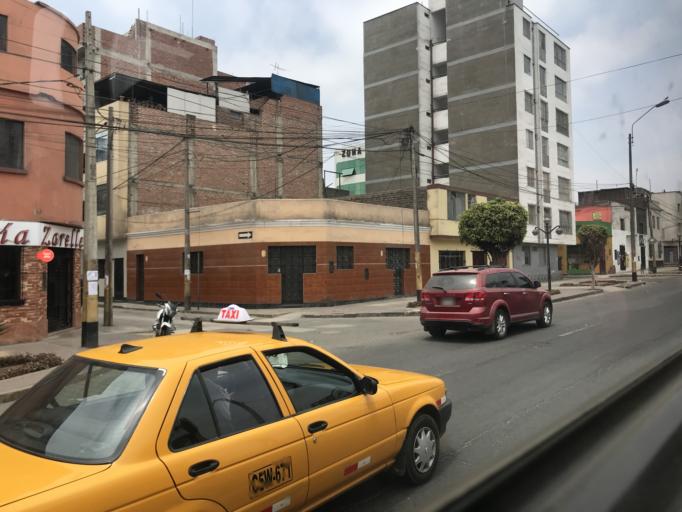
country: PE
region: Lima
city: Lima
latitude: -12.0570
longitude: -77.0513
